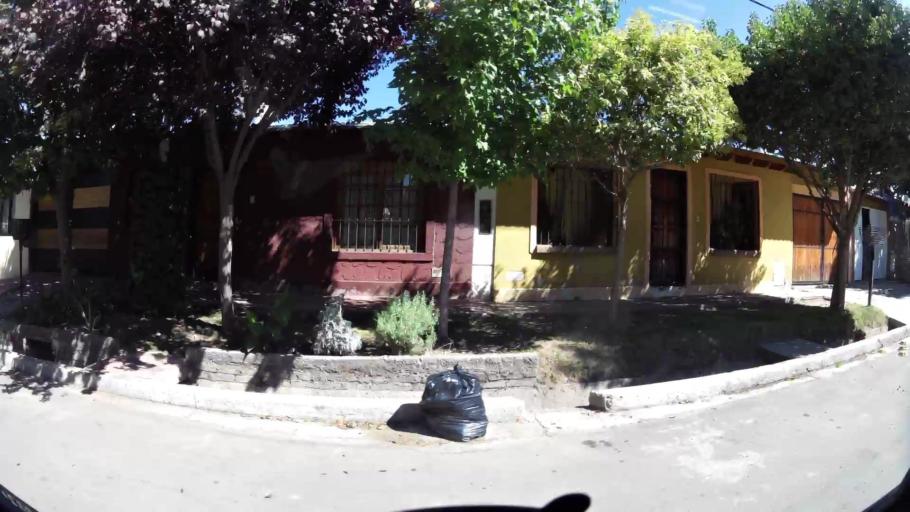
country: AR
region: Mendoza
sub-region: Departamento de Godoy Cruz
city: Godoy Cruz
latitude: -32.9673
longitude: -68.8363
